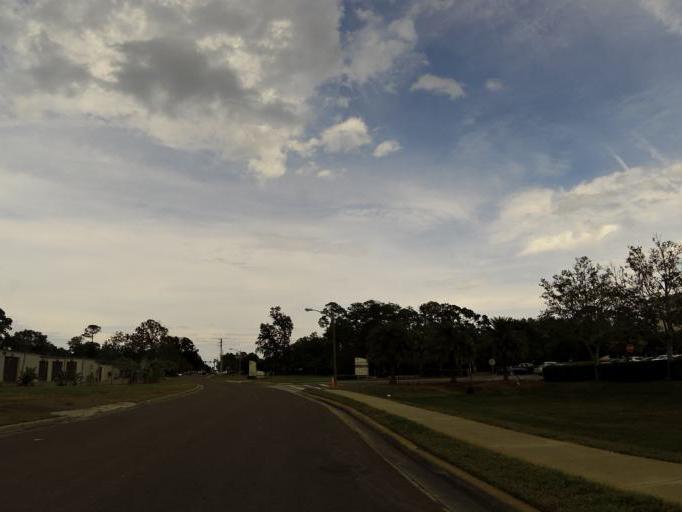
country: US
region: Florida
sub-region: Duval County
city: Jacksonville Beach
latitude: 30.2745
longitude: -81.3987
